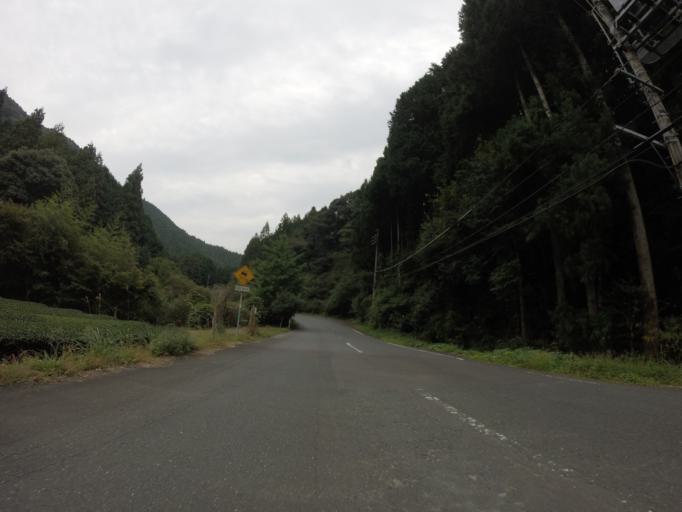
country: JP
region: Shizuoka
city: Mori
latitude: 34.8715
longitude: 138.0172
